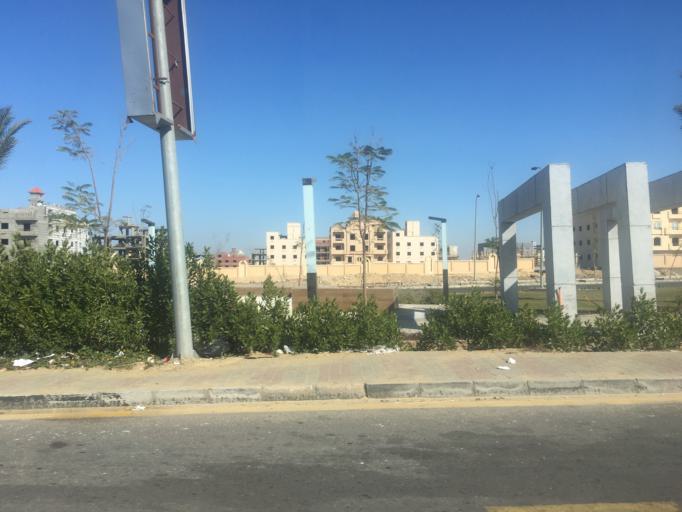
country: EG
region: Al Jizah
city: Awsim
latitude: 30.0149
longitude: 30.9768
